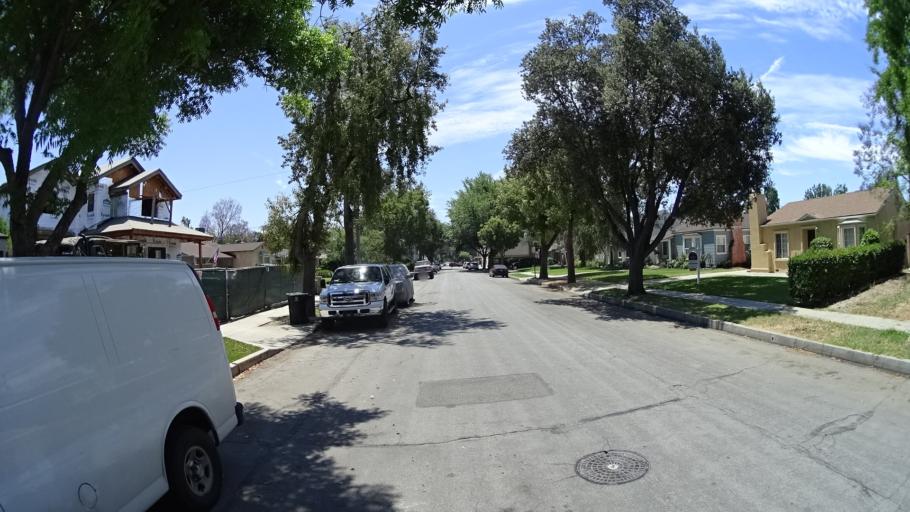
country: US
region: California
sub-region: Los Angeles County
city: Burbank
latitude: 34.1766
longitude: -118.3251
